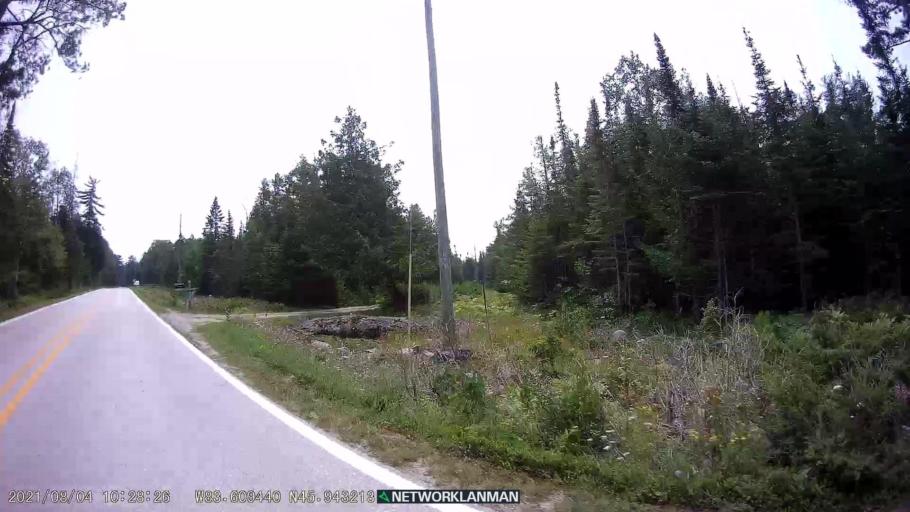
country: CA
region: Ontario
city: Thessalon
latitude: 45.9431
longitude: -83.6093
